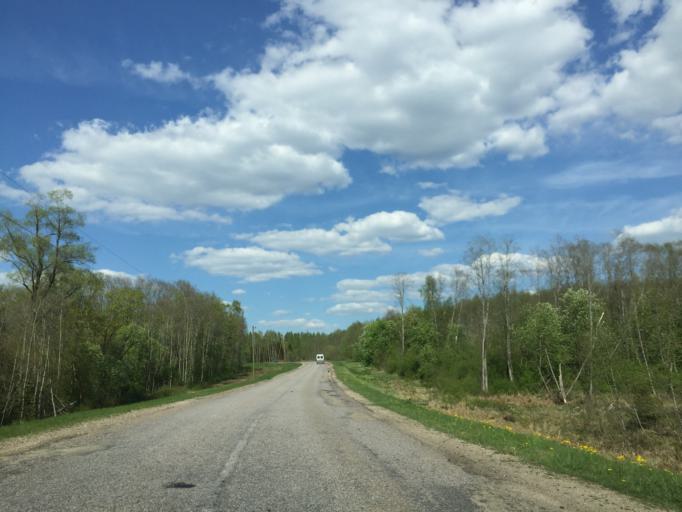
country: LV
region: Limbazu Rajons
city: Limbazi
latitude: 57.4397
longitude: 24.7200
